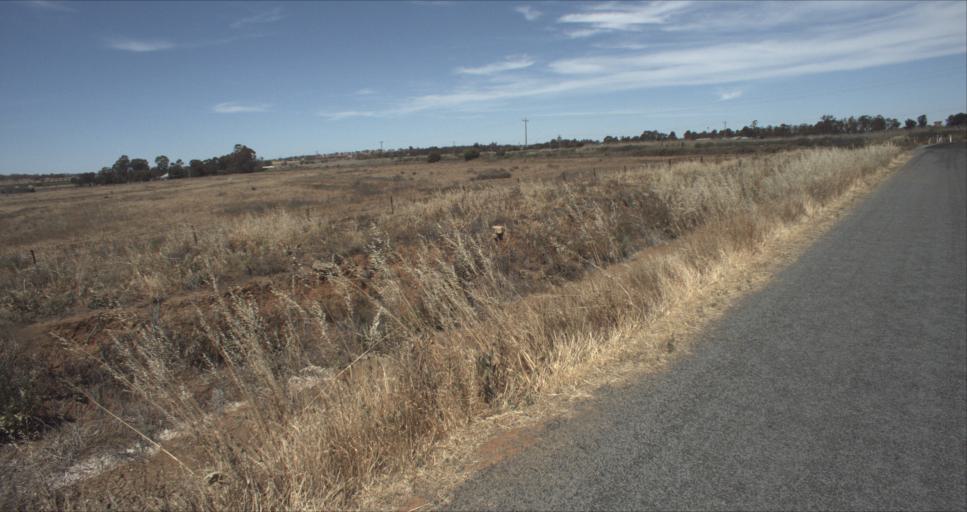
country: AU
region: New South Wales
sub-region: Leeton
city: Leeton
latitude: -34.6060
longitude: 146.4147
